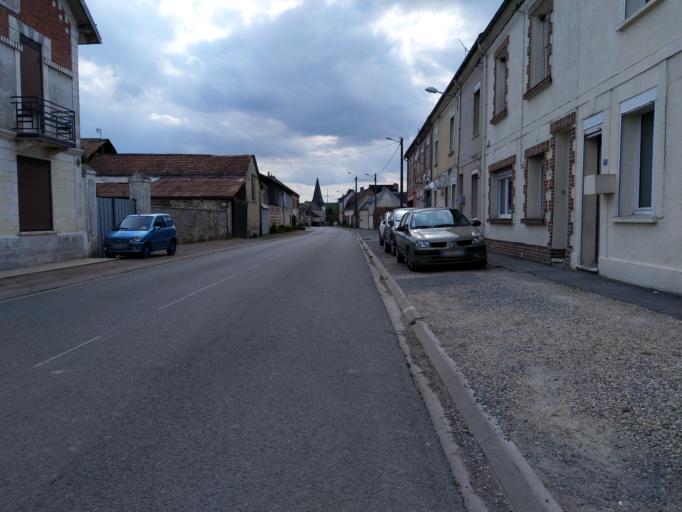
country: FR
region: Picardie
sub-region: Departement de l'Aisne
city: Guise
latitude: 49.9296
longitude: 3.5807
